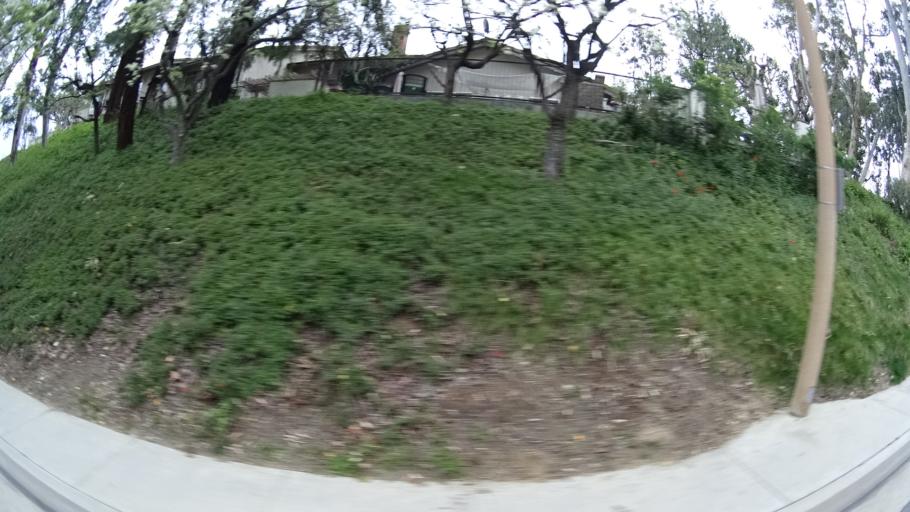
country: US
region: California
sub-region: Orange County
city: Villa Park
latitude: 33.8346
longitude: -117.7630
